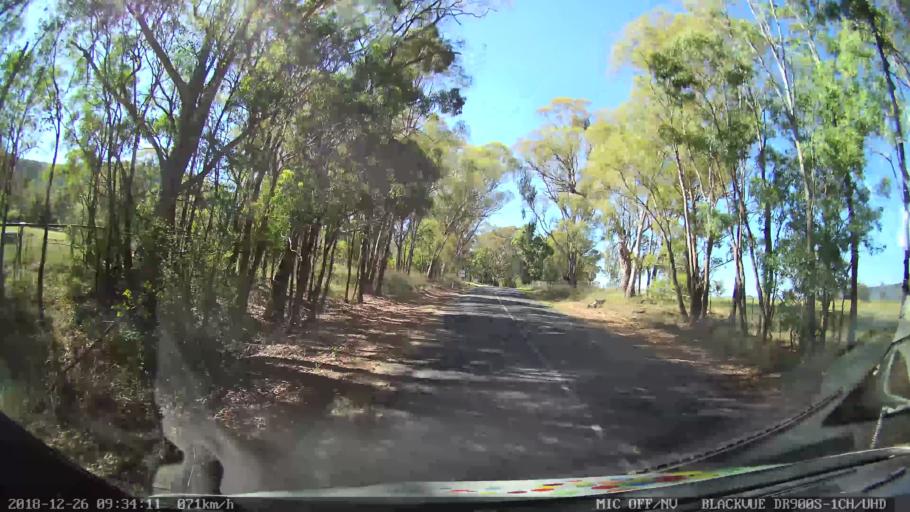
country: AU
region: New South Wales
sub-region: Mid-Western Regional
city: Kandos
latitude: -32.9025
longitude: 150.0375
